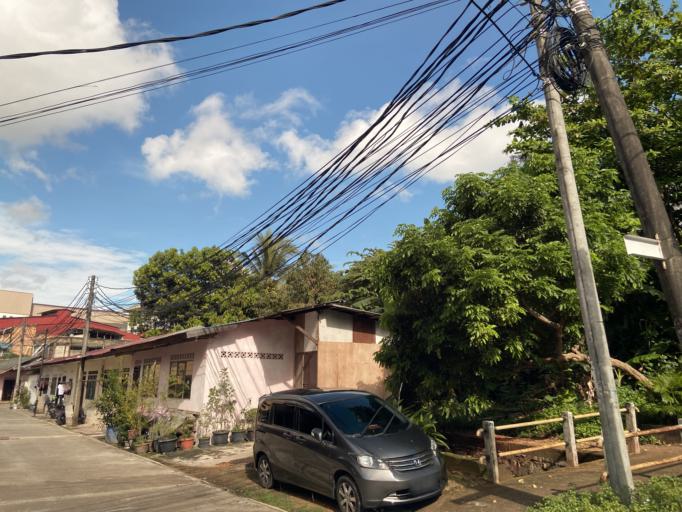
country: SG
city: Singapore
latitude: 1.1421
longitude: 104.0187
